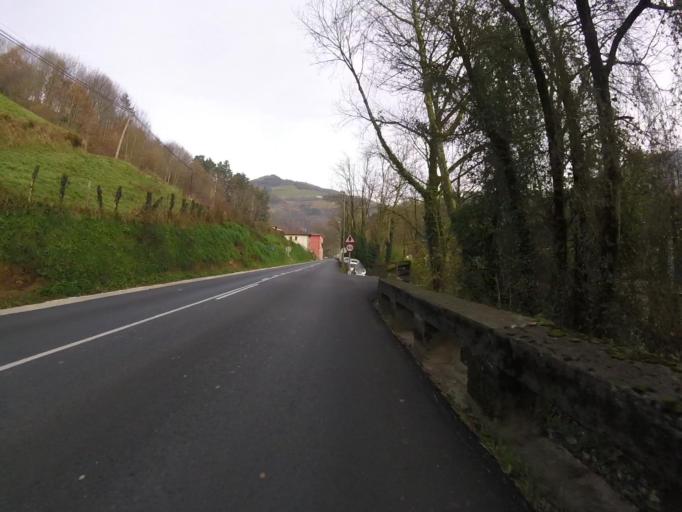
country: ES
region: Basque Country
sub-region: Provincia de Guipuzcoa
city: Belaunza
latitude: 43.1342
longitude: -2.0582
